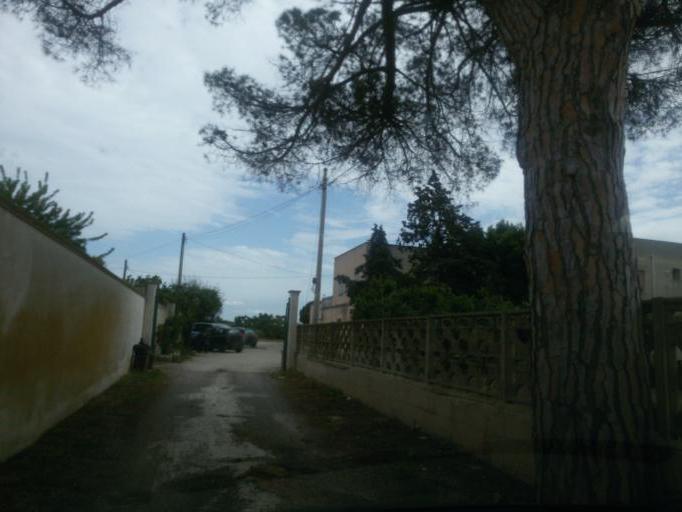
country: IT
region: Apulia
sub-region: Provincia di Brindisi
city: Brindisi
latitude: 40.6541
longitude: 17.9275
